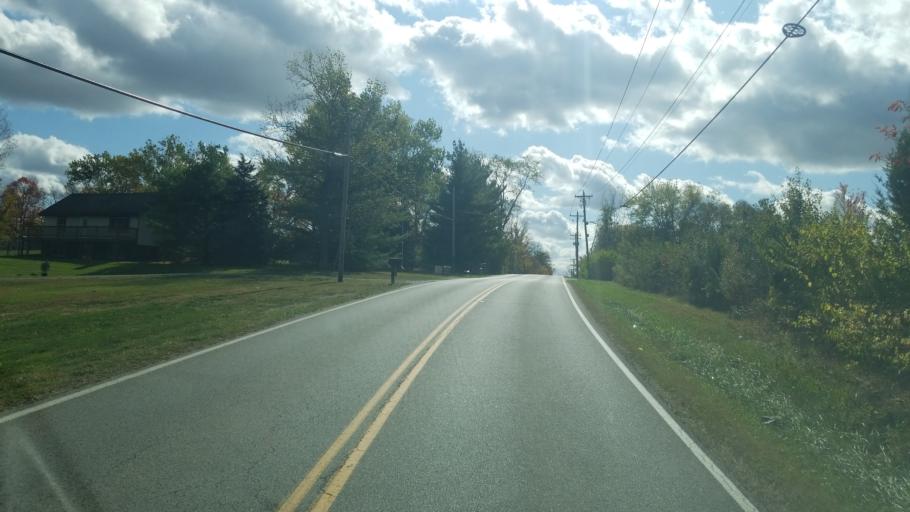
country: US
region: Ohio
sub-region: Warren County
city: Lebanon
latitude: 39.3998
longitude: -84.1747
